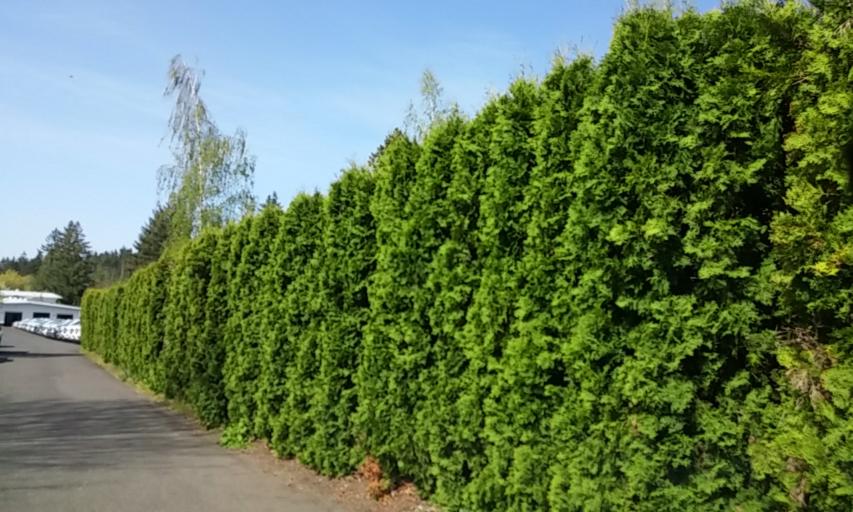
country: US
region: Oregon
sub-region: Washington County
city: West Slope
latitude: 45.4980
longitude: -122.7691
